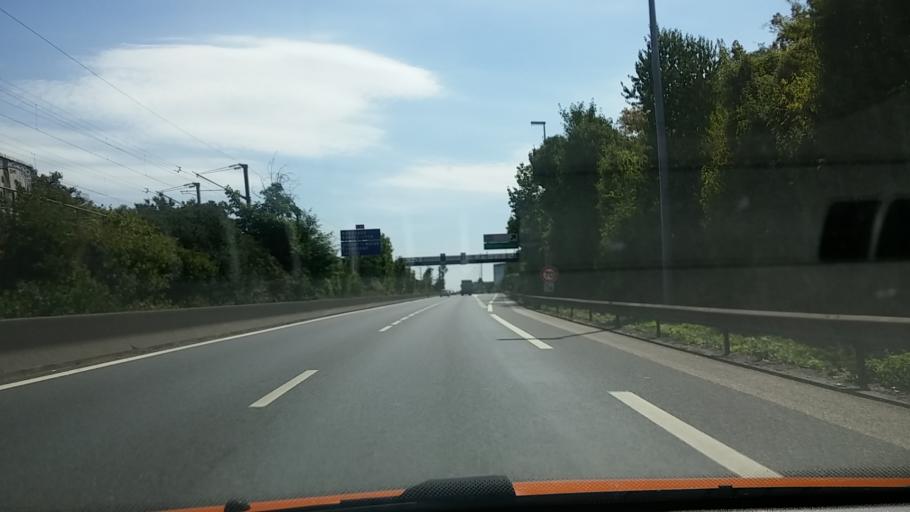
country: FR
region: Ile-de-France
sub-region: Departement du Val-de-Marne
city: Fontenay-sous-Bois
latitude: 48.8575
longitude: 2.4876
